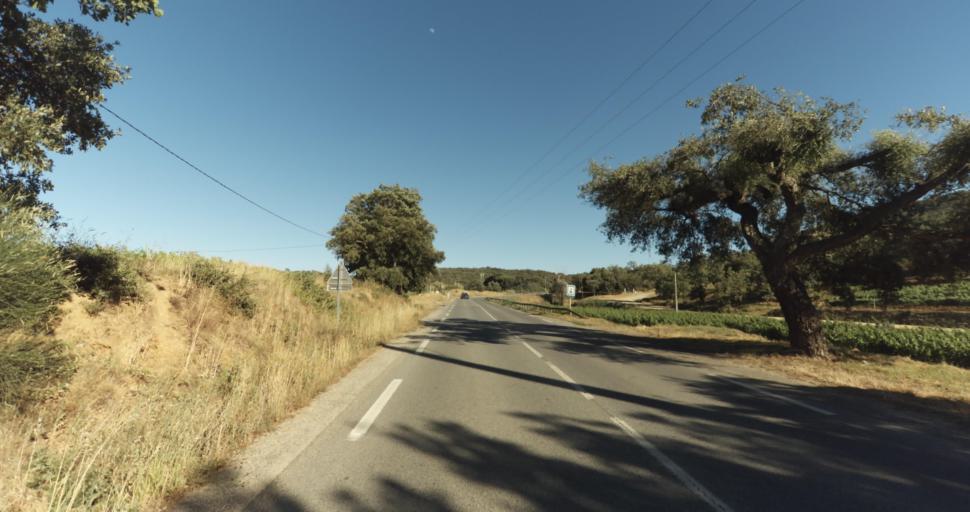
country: FR
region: Provence-Alpes-Cote d'Azur
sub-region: Departement du Var
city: Ramatuelle
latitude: 43.2365
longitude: 6.6092
